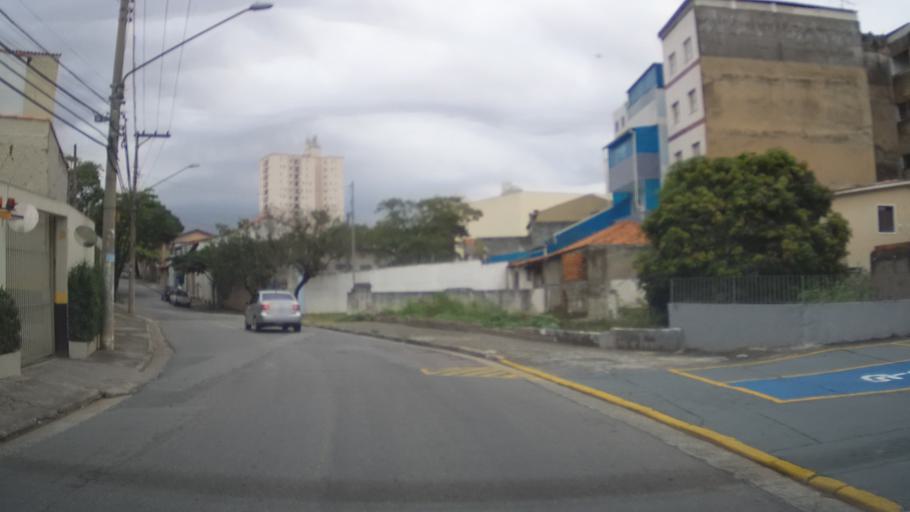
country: BR
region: Sao Paulo
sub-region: Guarulhos
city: Guarulhos
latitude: -23.4574
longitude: -46.5558
